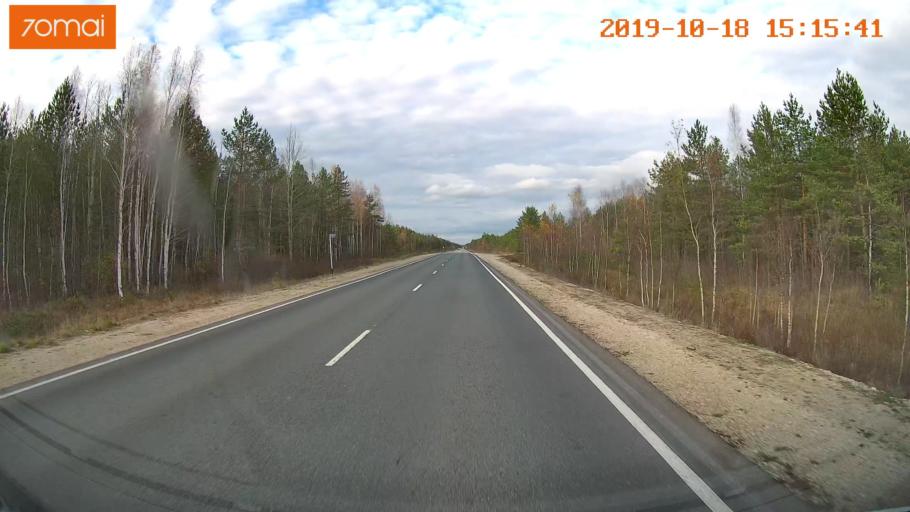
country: RU
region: Vladimir
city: Gus'-Khrustal'nyy
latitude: 55.6233
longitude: 40.7231
